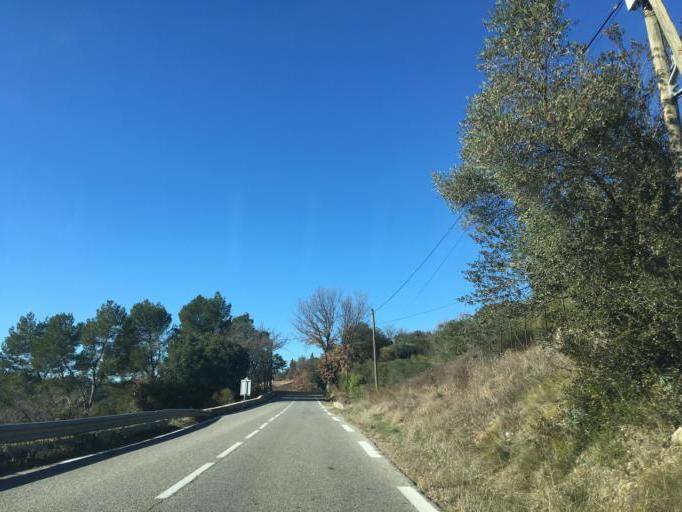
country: FR
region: Provence-Alpes-Cote d'Azur
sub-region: Departement du Var
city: Barjols
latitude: 43.5996
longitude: 5.9550
